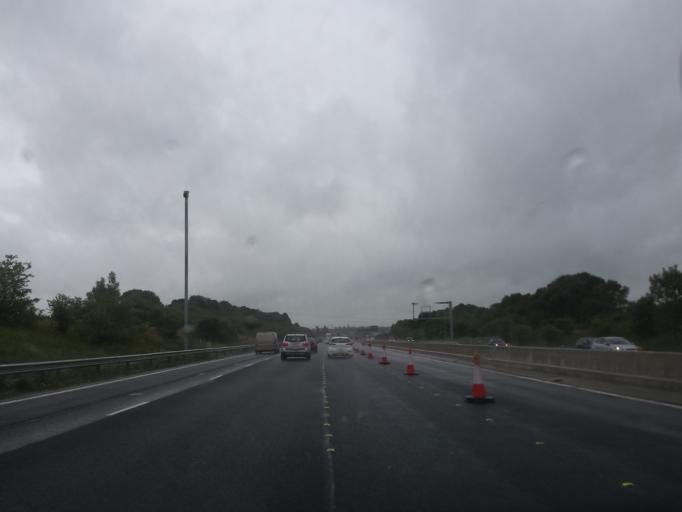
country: GB
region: England
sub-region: Rotherham
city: Wales
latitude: 53.3604
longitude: -1.2836
